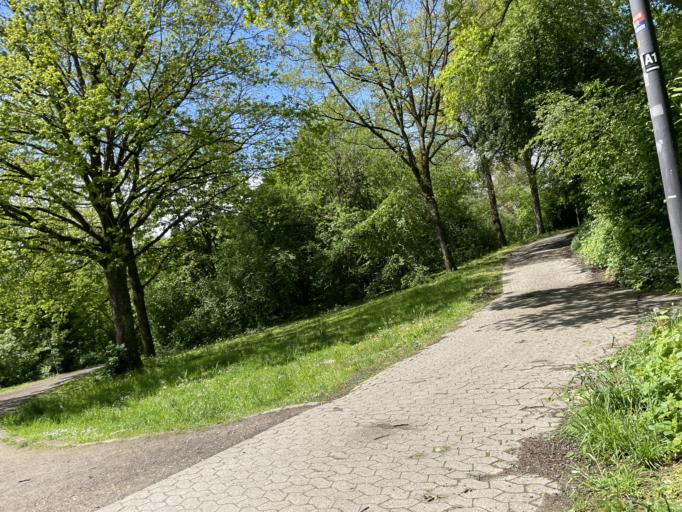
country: DE
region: North Rhine-Westphalia
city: Haan
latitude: 51.1974
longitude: 7.0196
